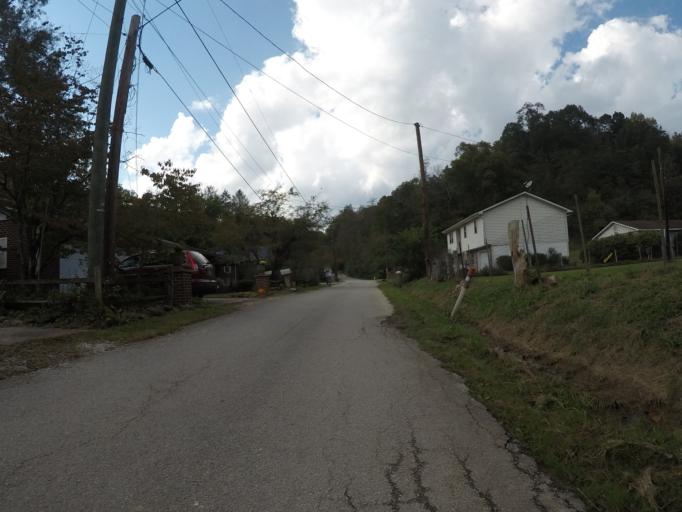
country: US
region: West Virginia
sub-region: Wayne County
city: Lavalette
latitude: 38.3503
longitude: -82.4535
